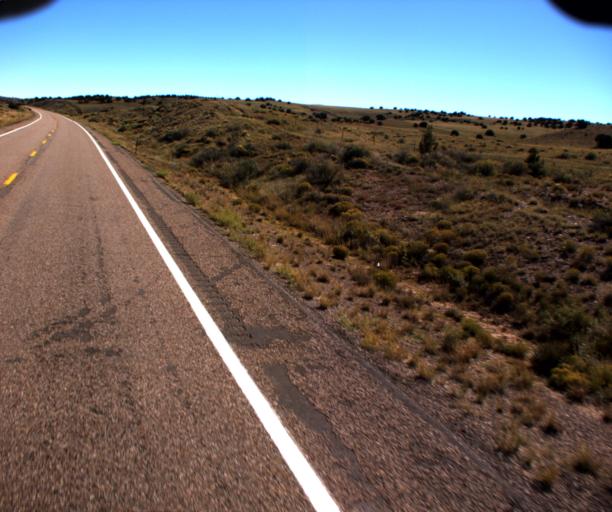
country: US
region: Arizona
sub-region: Apache County
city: Saint Johns
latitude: 34.5850
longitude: -109.5682
